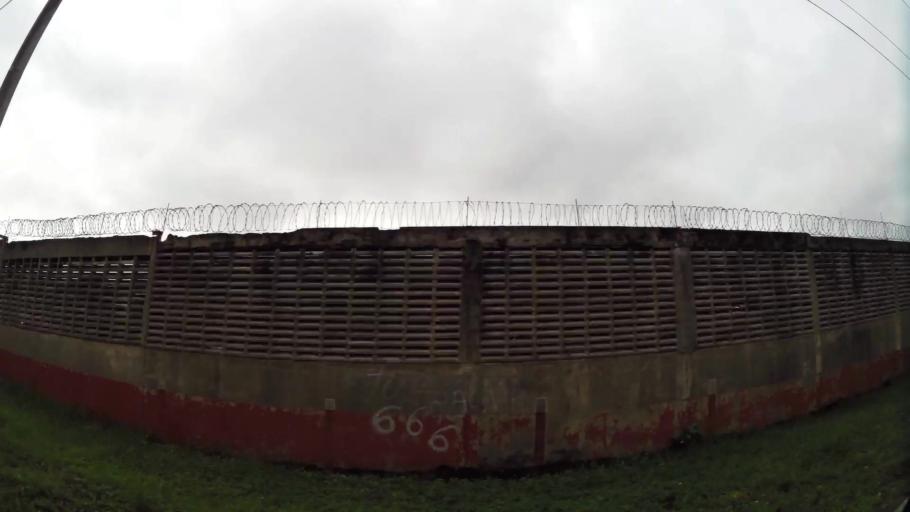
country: PA
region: Panama
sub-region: Distrito de Panama
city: Ancon
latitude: 8.9752
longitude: -79.5388
